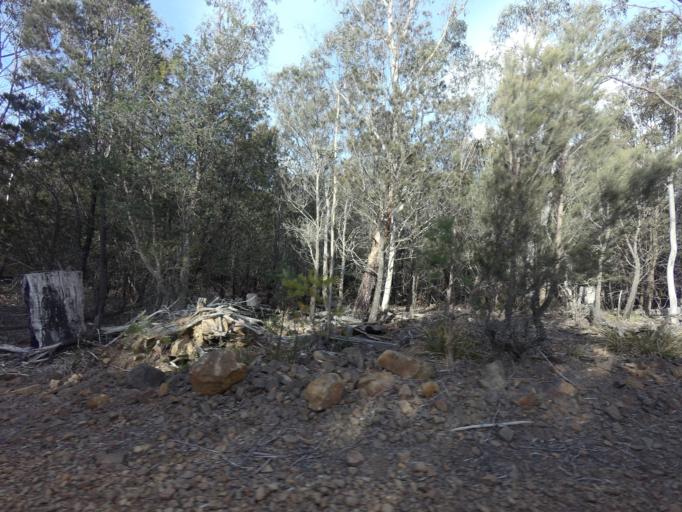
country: AU
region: Tasmania
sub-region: Break O'Day
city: St Helens
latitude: -41.8423
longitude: 148.0871
